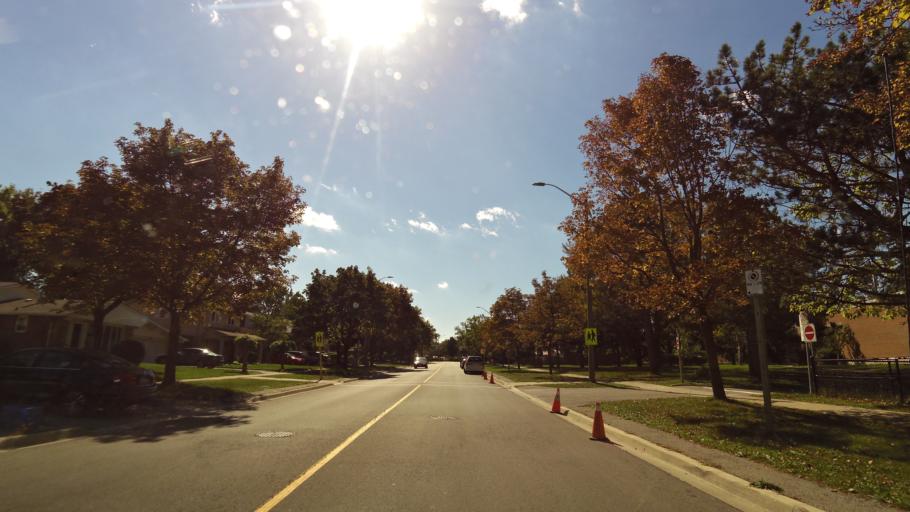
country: CA
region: Ontario
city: Mississauga
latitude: 43.5889
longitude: -79.6198
